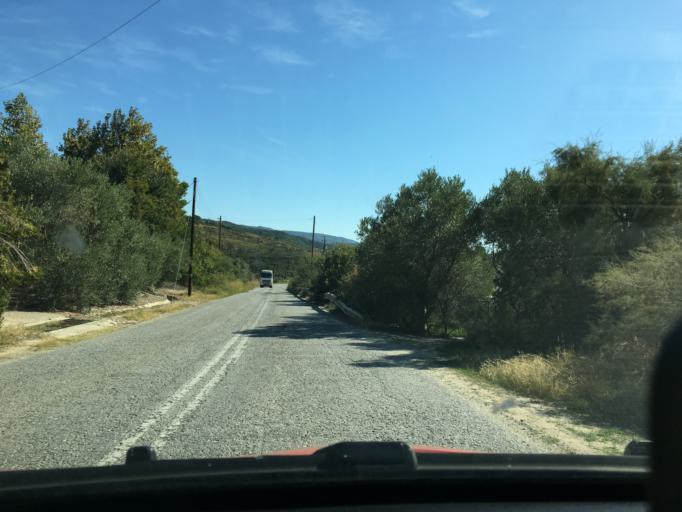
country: GR
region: Central Macedonia
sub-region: Nomos Chalkidikis
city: Ouranoupolis
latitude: 40.3527
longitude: 23.9529
